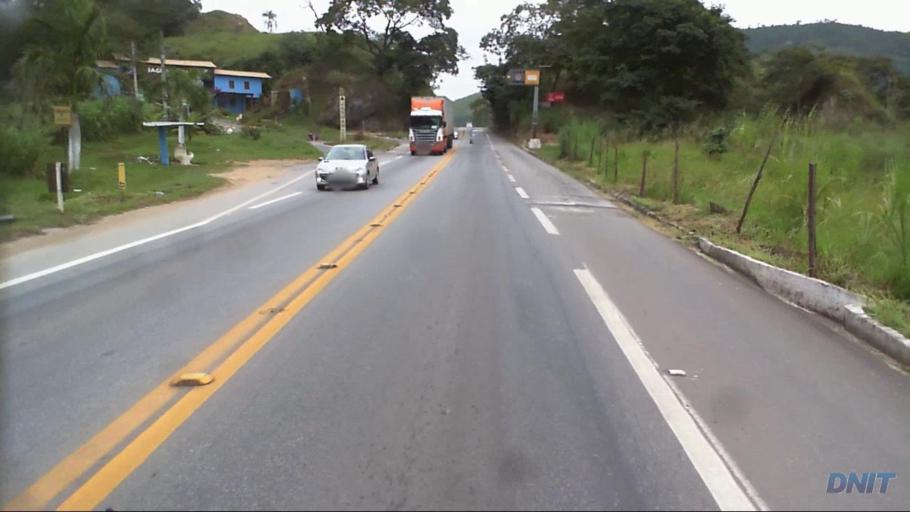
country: BR
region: Minas Gerais
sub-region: Timoteo
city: Timoteo
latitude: -19.6066
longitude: -42.7603
